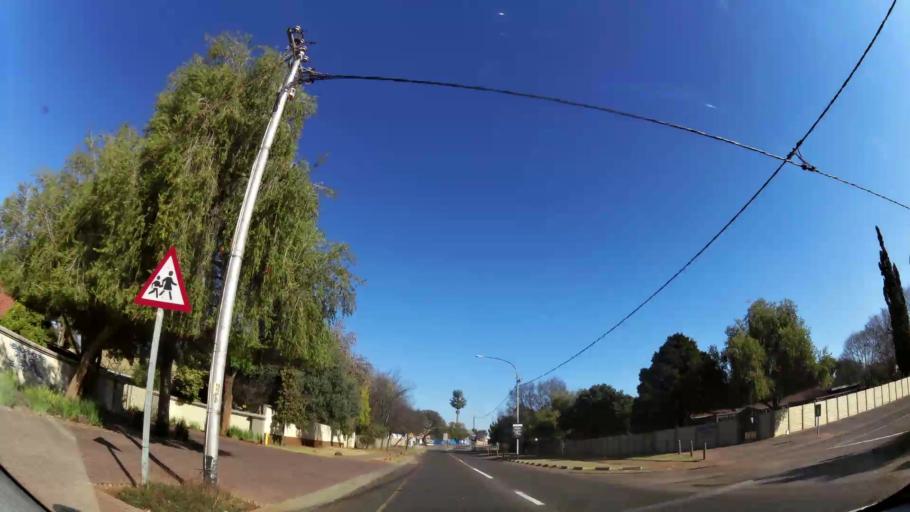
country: ZA
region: Gauteng
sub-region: City of Tshwane Metropolitan Municipality
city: Centurion
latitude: -25.8506
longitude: 28.1700
